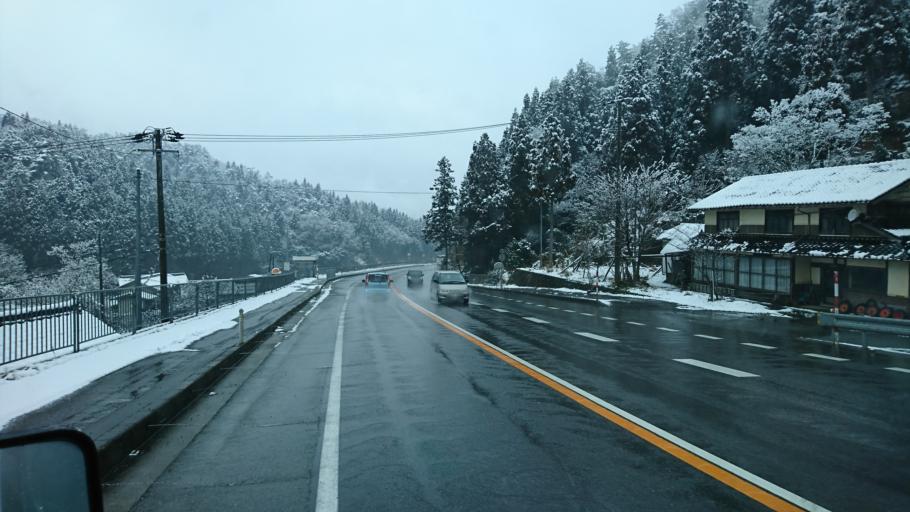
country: JP
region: Hyogo
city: Toyooka
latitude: 35.4075
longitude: 134.6036
